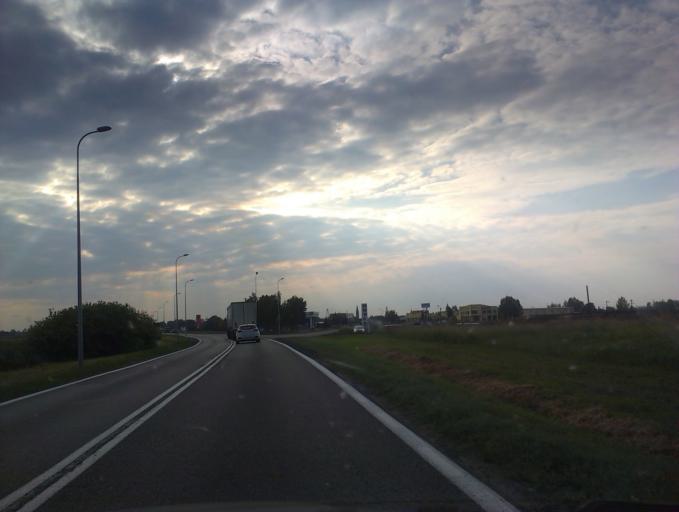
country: PL
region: Lower Silesian Voivodeship
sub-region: Powiat trzebnicki
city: Prusice
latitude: 51.3633
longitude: 16.9785
